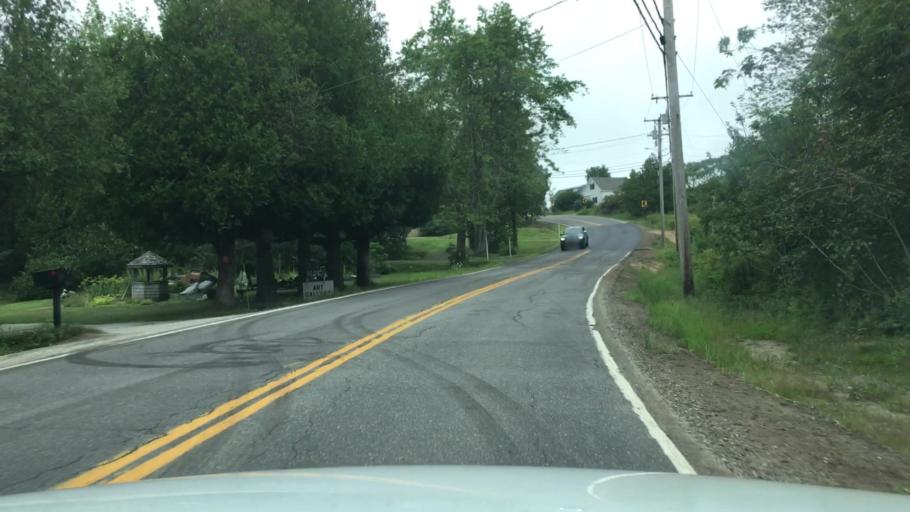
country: US
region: Maine
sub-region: Cumberland County
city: Harpswell Center
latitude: 43.7842
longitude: -69.9507
